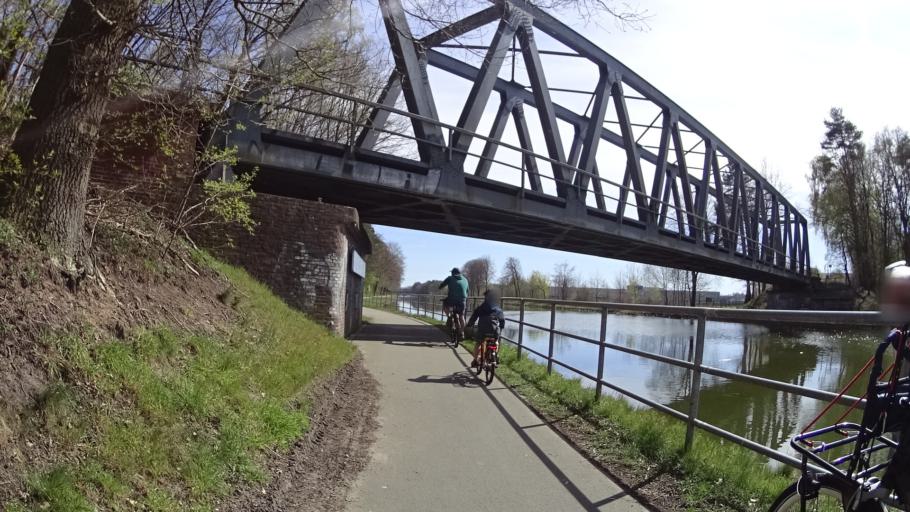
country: DE
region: Lower Saxony
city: Spelle
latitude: 52.3271
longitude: 7.4525
